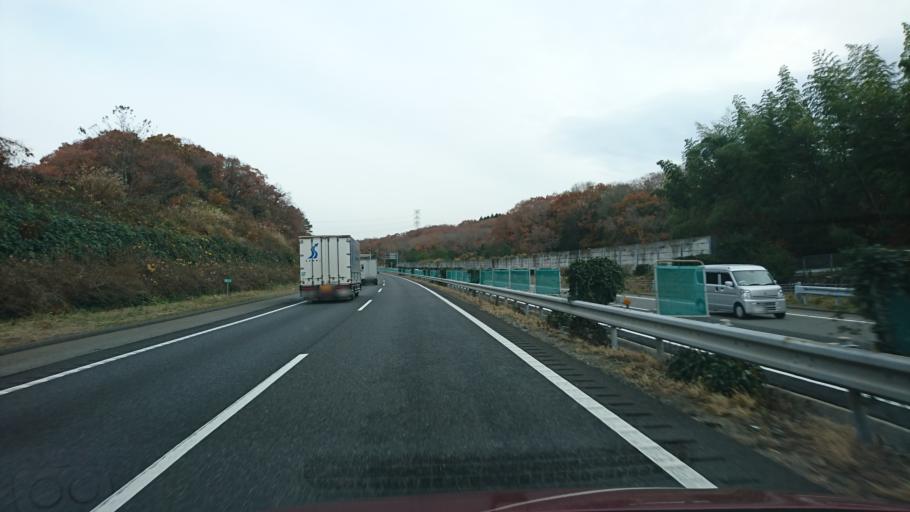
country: JP
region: Hyogo
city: Sandacho
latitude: 34.8289
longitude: 135.1833
